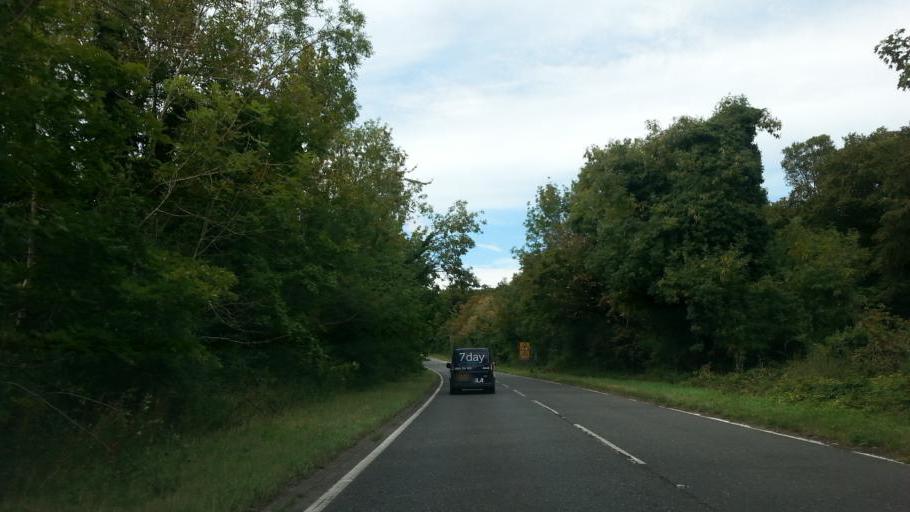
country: GB
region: England
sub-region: Cambridgeshire
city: Sawston
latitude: 52.1551
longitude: 0.1840
